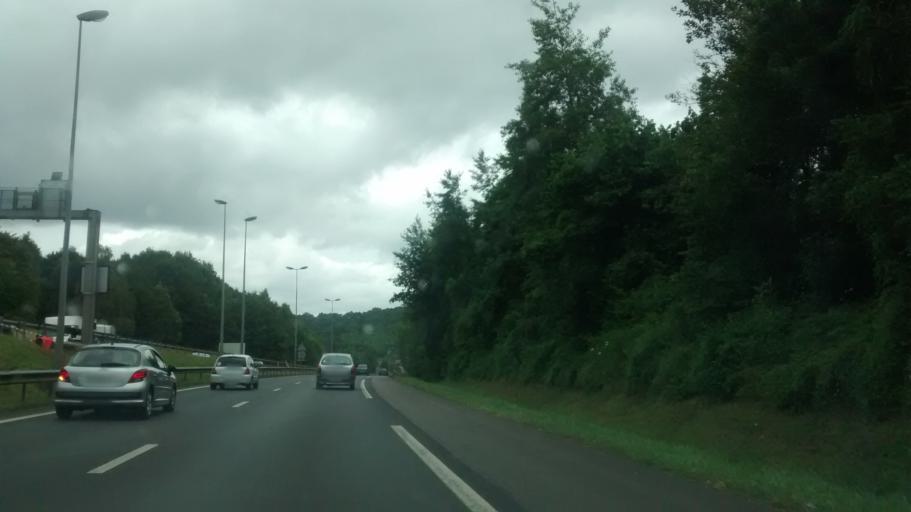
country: FR
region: Haute-Normandie
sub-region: Departement de la Seine-Maritime
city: Darnetal
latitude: 49.4530
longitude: 1.1452
